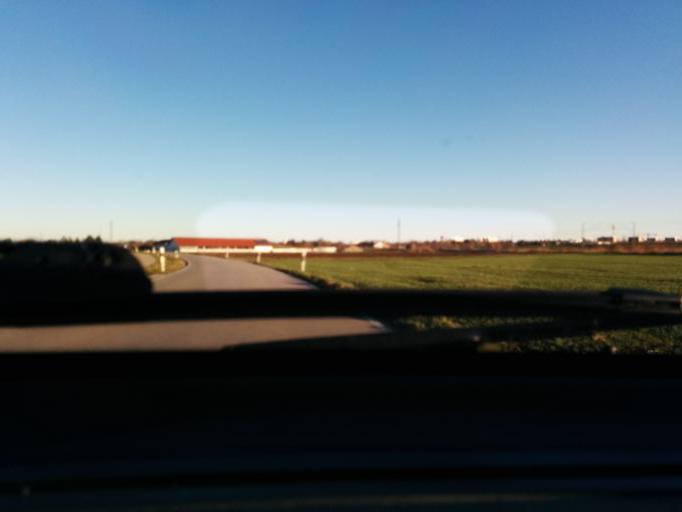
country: DE
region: Bavaria
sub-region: Upper Bavaria
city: Germering
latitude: 48.1605
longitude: 11.3956
